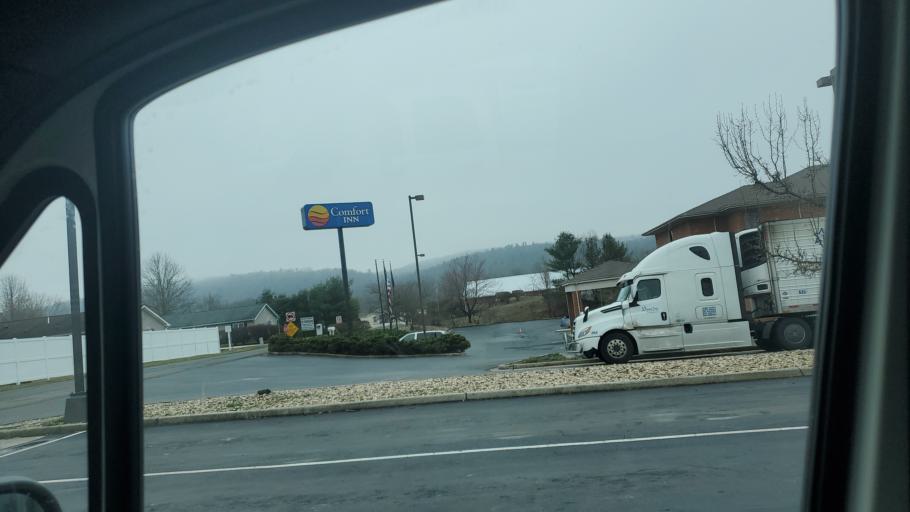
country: US
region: Pennsylvania
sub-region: Schuylkill County
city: Pine Grove
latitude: 40.5341
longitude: -76.4260
